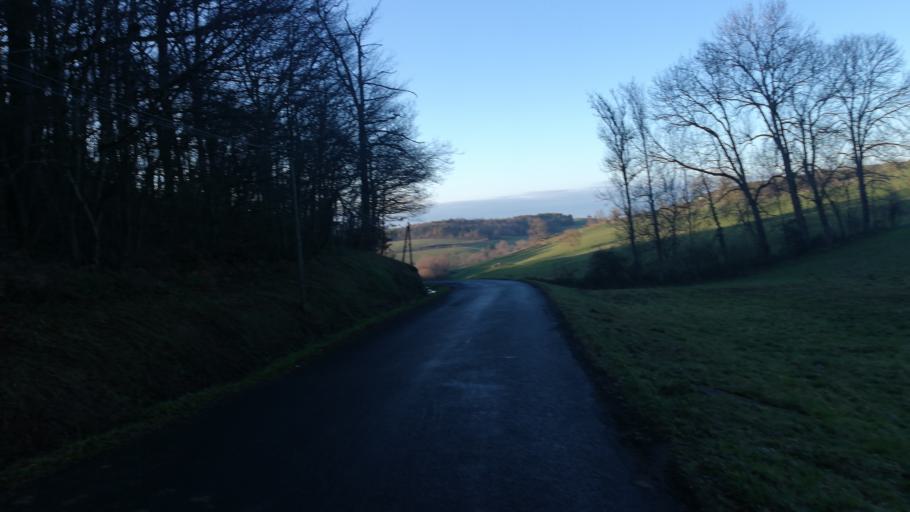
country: FR
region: Auvergne
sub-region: Departement du Puy-de-Dome
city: Billom
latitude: 45.6858
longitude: 3.3787
